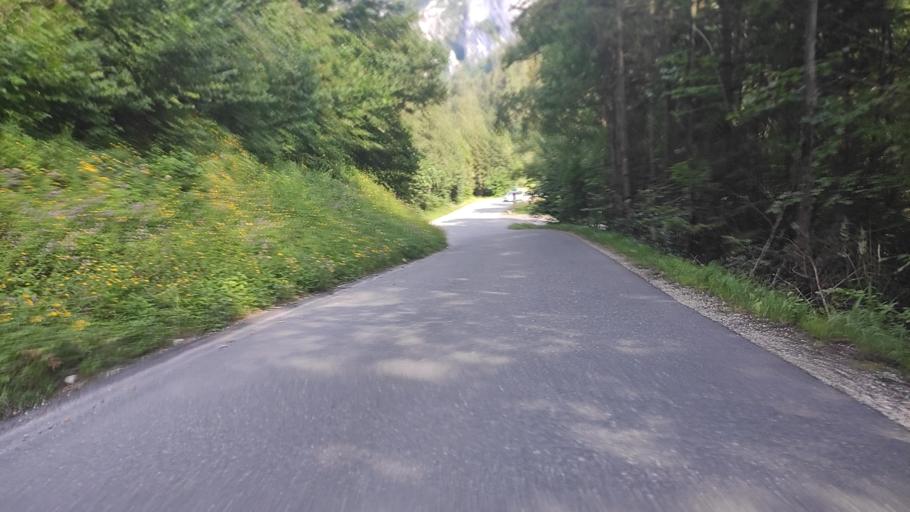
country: AT
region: Salzburg
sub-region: Politischer Bezirk Zell am See
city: Unken
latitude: 47.6641
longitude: 12.7547
